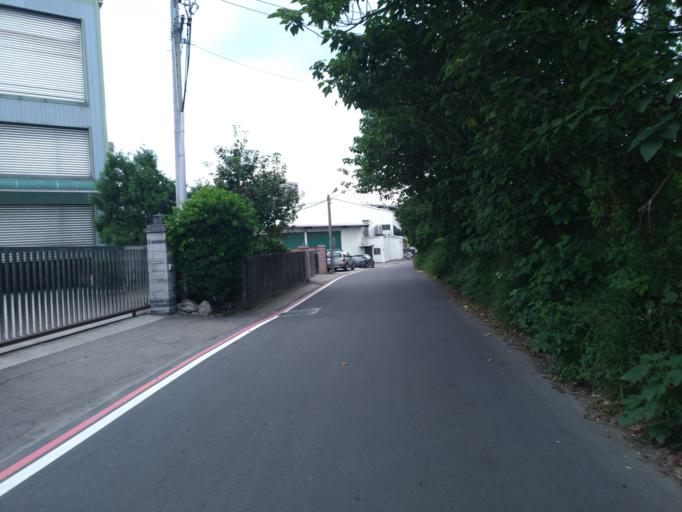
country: TW
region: Taiwan
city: Daxi
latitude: 24.9138
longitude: 121.1702
